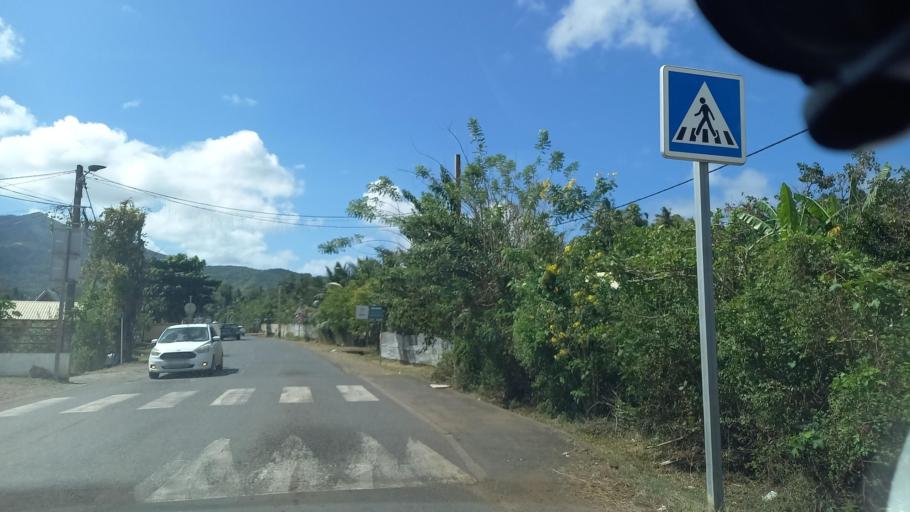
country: YT
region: Chirongui
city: Chirongui
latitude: -12.9224
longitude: 45.1575
